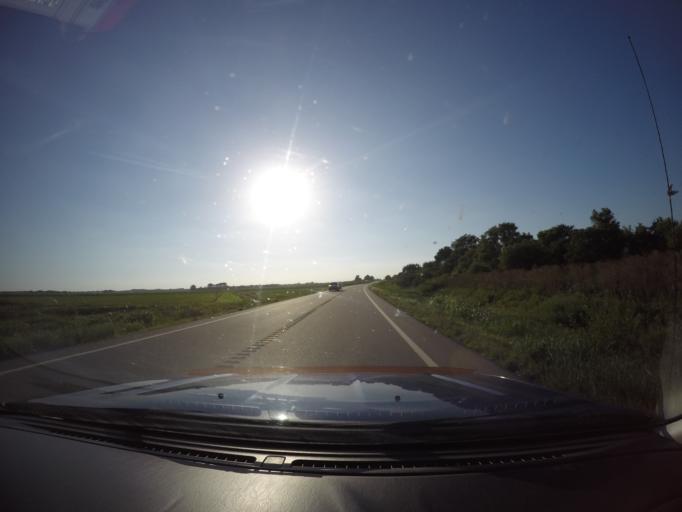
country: US
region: Kansas
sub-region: Shawnee County
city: Rossville
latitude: 39.1219
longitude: -95.9249
